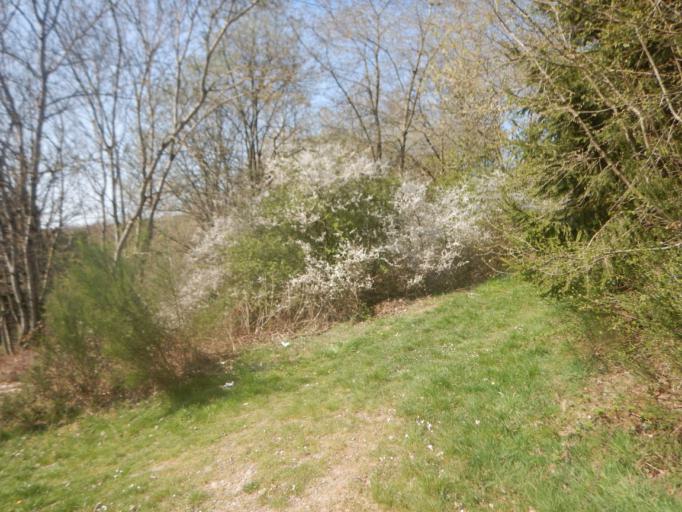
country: LU
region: Diekirch
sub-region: Canton de Clervaux
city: Clervaux
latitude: 50.0582
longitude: 5.9990
